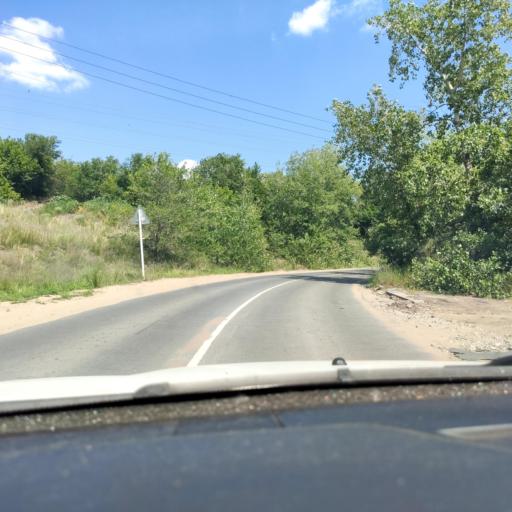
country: RU
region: Samara
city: Pribrezhnyy
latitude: 53.4835
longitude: 49.8424
